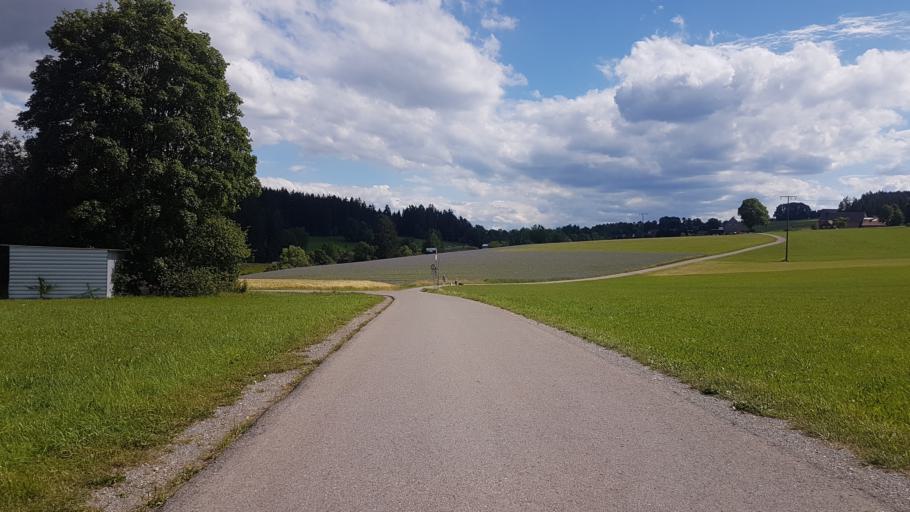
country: DE
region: Baden-Wuerttemberg
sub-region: Freiburg Region
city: Konigsfeld im Schwarzwald
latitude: 48.1574
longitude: 8.4092
